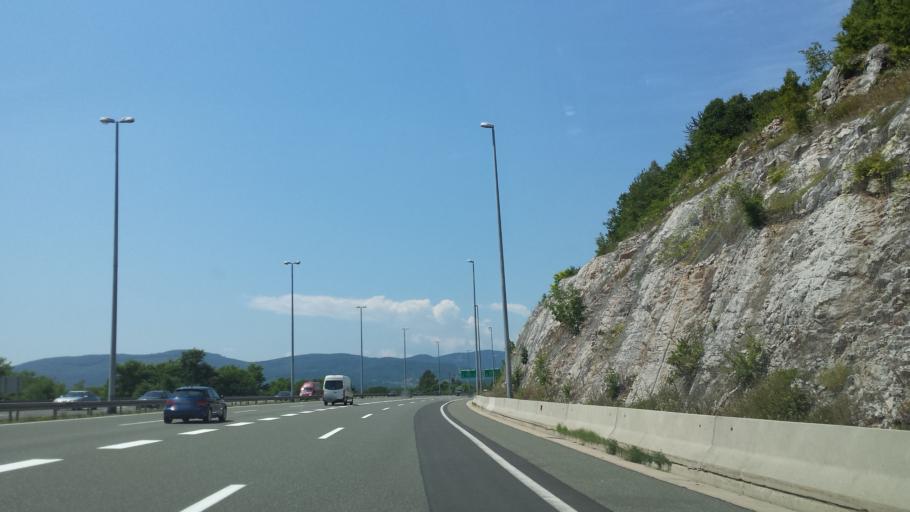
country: HR
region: Karlovacka
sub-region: Grad Ogulin
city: Ogulin
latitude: 45.4103
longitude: 15.2750
